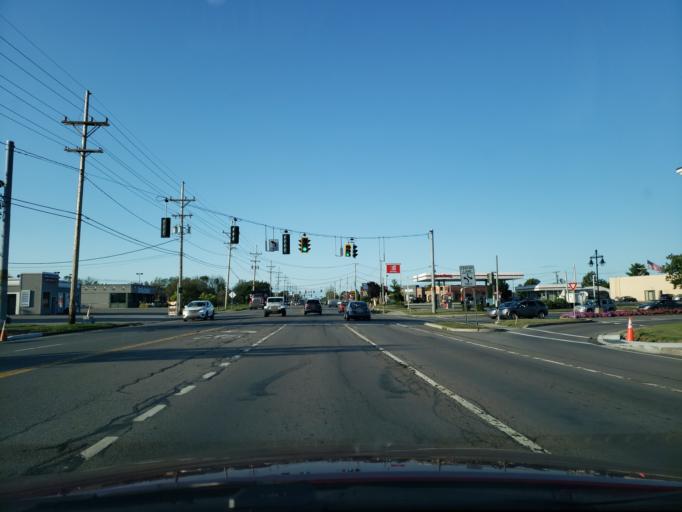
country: US
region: New York
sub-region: Monroe County
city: Brighton
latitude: 43.1905
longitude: -77.5035
